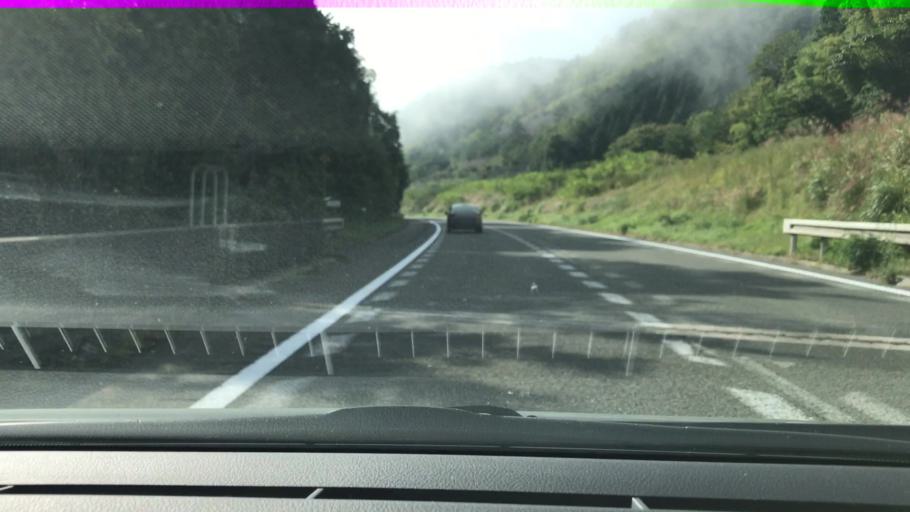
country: JP
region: Hyogo
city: Sasayama
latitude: 35.1114
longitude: 135.1661
